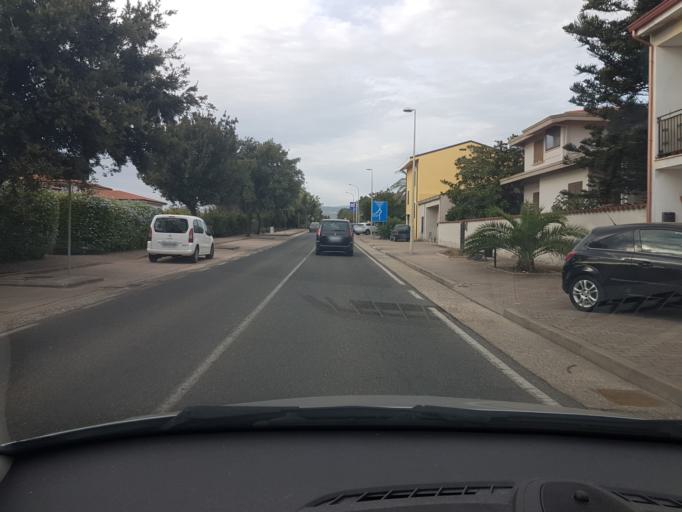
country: IT
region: Sardinia
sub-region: Provincia di Oristano
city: Nurachi
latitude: 39.9798
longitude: 8.5388
